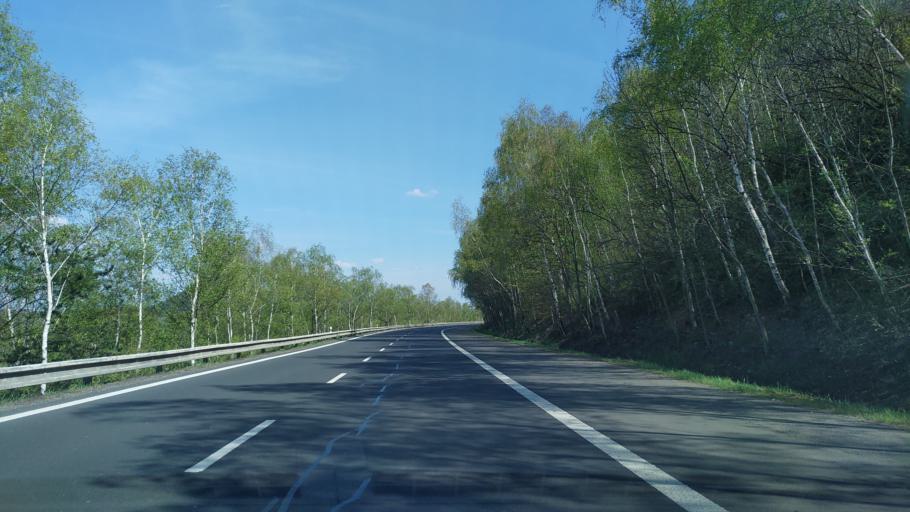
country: CZ
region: Ustecky
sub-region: Okres Most
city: Most
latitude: 50.5238
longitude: 13.6341
